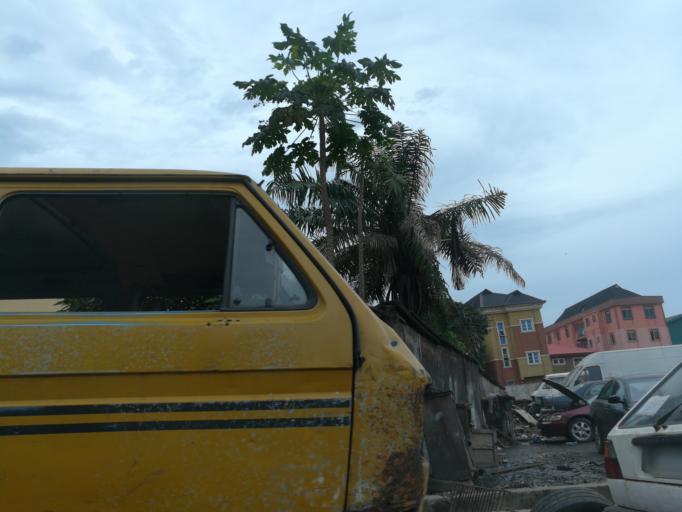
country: NG
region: Lagos
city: Ebute Metta
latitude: 6.4868
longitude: 3.3881
